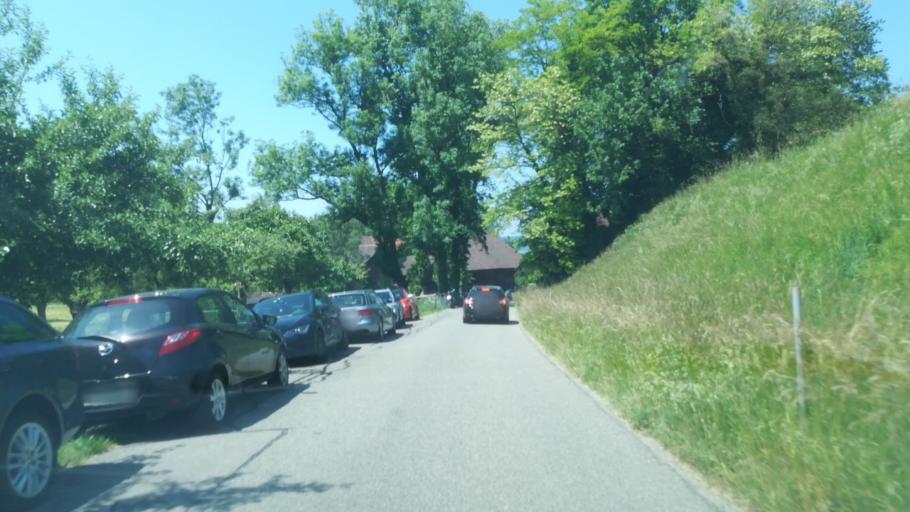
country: CH
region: Thurgau
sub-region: Frauenfeld District
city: Pfyn
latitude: 47.6291
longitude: 8.9268
